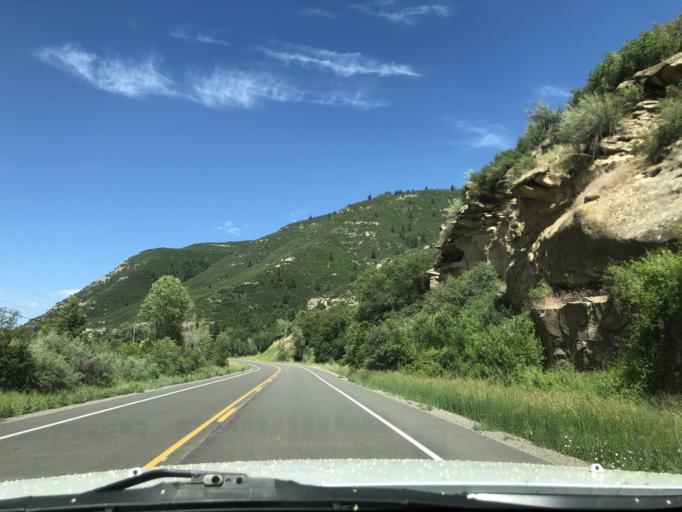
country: US
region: Colorado
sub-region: Delta County
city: Paonia
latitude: 38.9383
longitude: -107.3772
